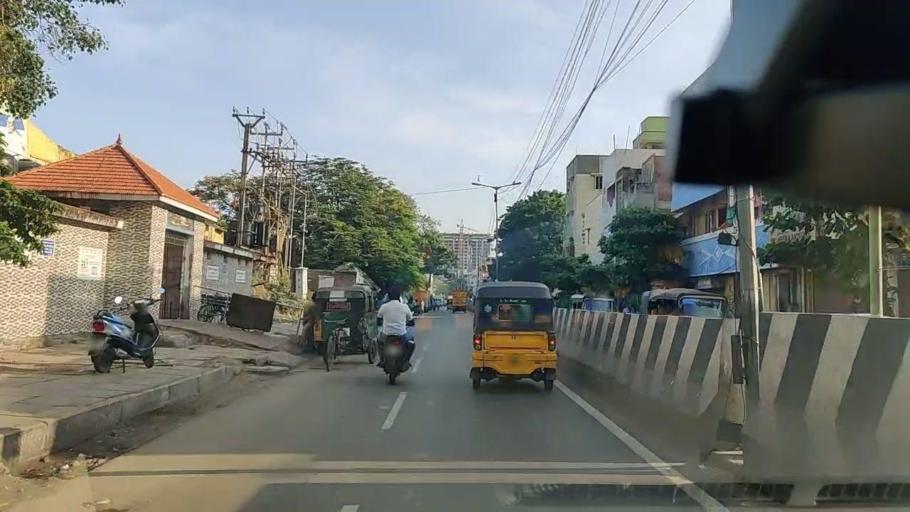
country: IN
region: Tamil Nadu
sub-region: Chennai
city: George Town
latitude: 13.0961
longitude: 80.2752
